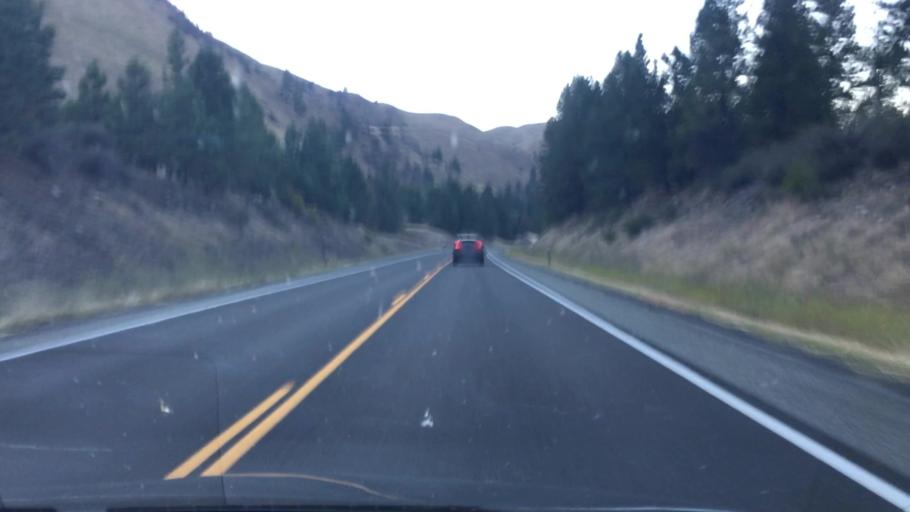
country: US
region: Idaho
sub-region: Valley County
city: McCall
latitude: 45.3011
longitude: -116.3612
